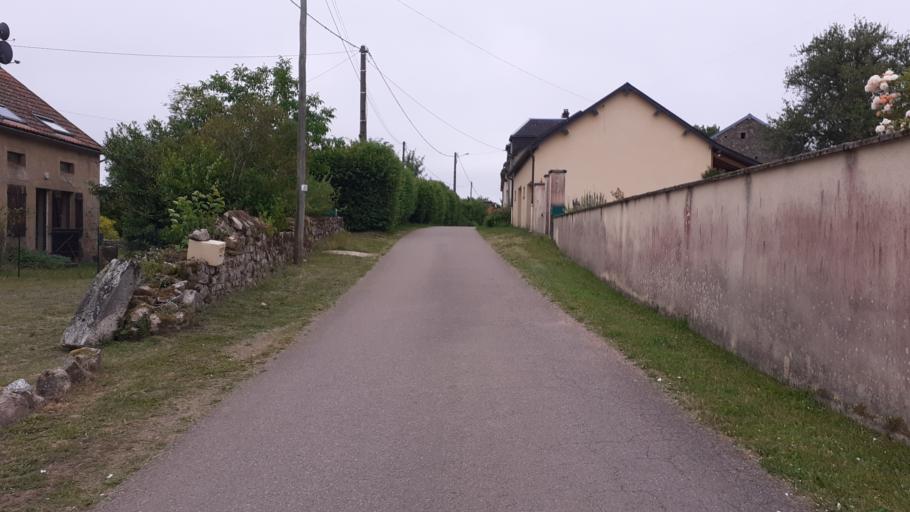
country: FR
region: Bourgogne
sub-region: Departement de la Cote-d'Or
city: Saulieu
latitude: 47.2702
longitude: 4.1348
